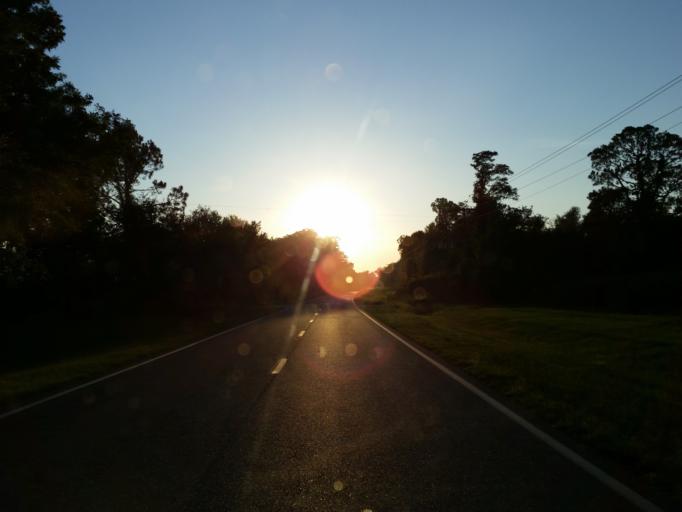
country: US
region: Georgia
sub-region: Berrien County
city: Nashville
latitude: 31.1871
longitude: -83.1945
